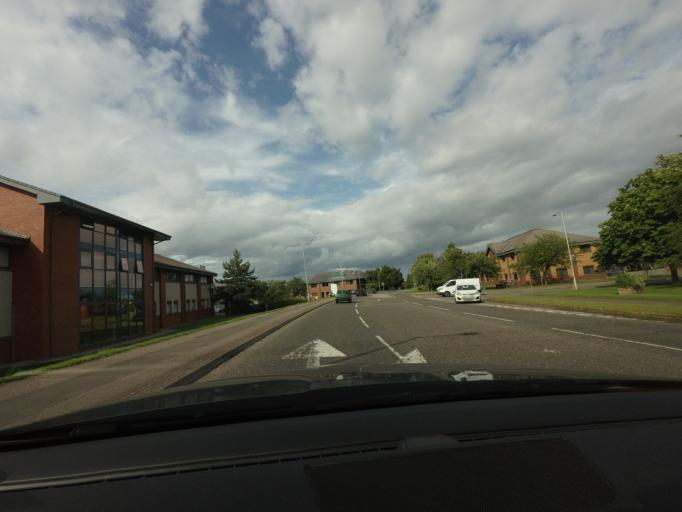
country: GB
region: Scotland
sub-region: Highland
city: Inverness
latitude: 57.4730
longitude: -4.1894
